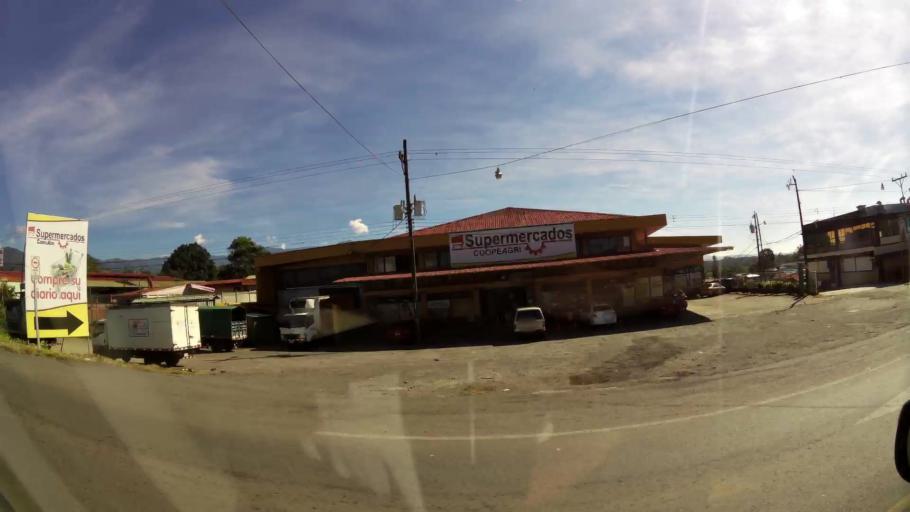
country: CR
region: San Jose
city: San Isidro
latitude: 9.3857
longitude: -83.7070
